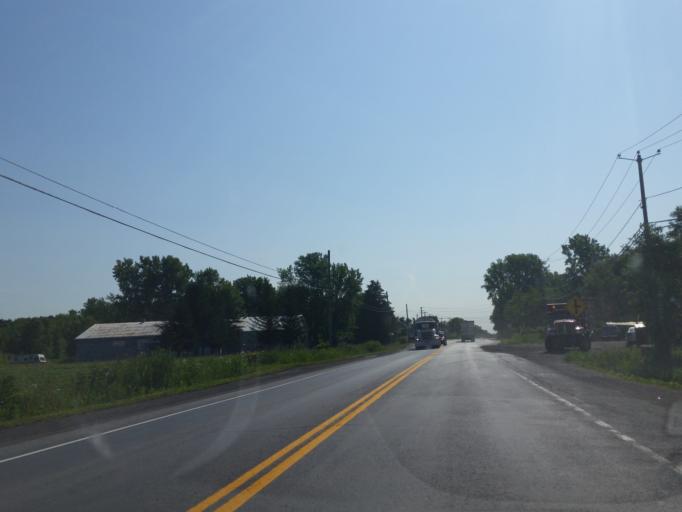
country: CA
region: Quebec
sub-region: Monteregie
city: Saint-Jean-sur-Richelieu
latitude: 45.3034
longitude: -73.3151
